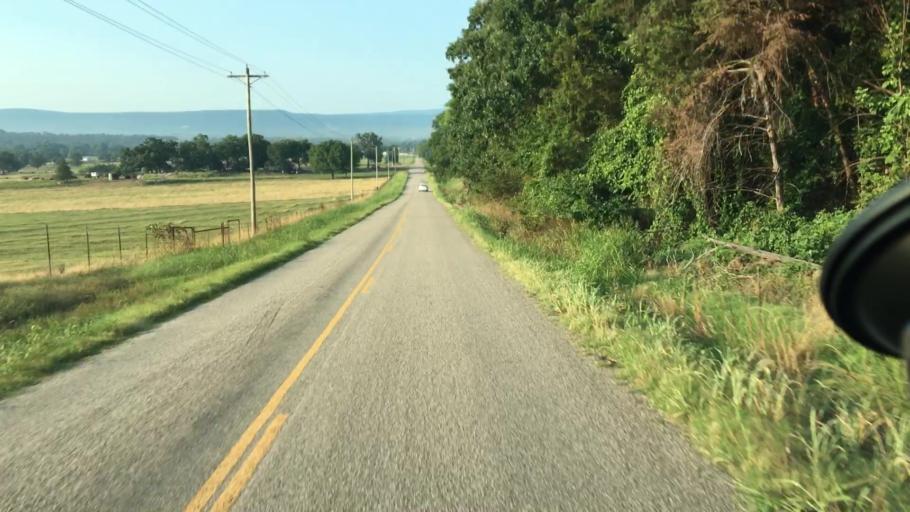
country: US
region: Arkansas
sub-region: Johnson County
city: Coal Hill
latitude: 35.3496
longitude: -93.6134
